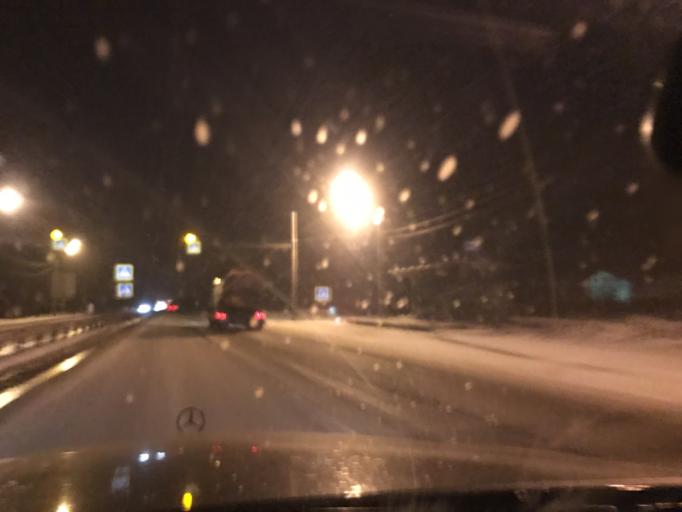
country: RU
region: Moskovskaya
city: Noginsk
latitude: 55.8567
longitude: 38.5287
